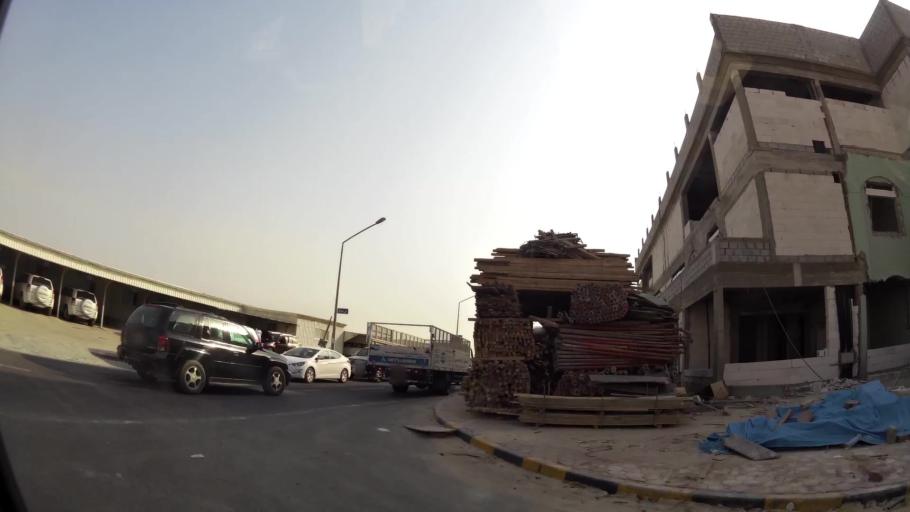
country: KW
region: Al Asimah
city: Ar Rabiyah
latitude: 29.3345
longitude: 47.8052
